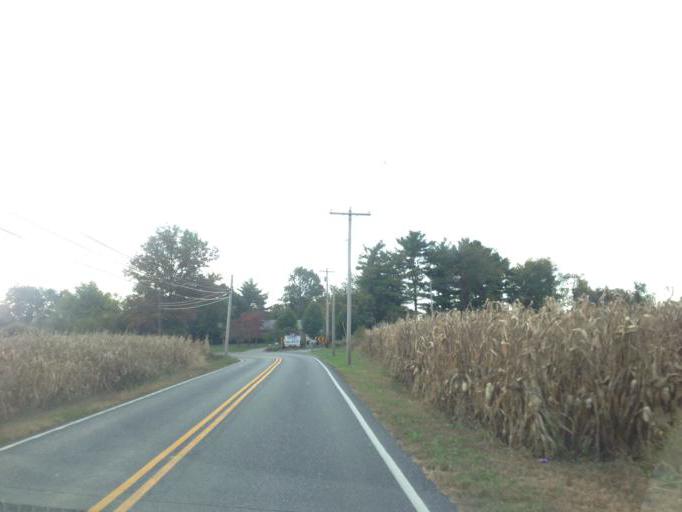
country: US
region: Maryland
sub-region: Carroll County
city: Mount Airy
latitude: 39.3455
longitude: -77.1695
